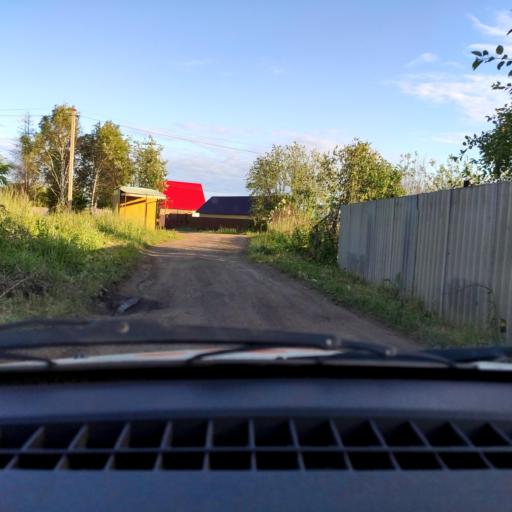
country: RU
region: Bashkortostan
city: Mikhaylovka
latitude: 54.9278
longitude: 55.7562
